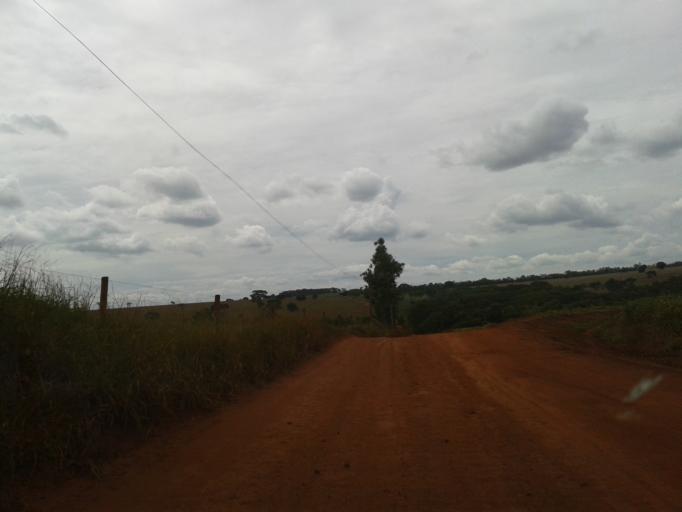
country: BR
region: Minas Gerais
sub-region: Centralina
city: Centralina
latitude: -18.7725
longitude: -49.2207
